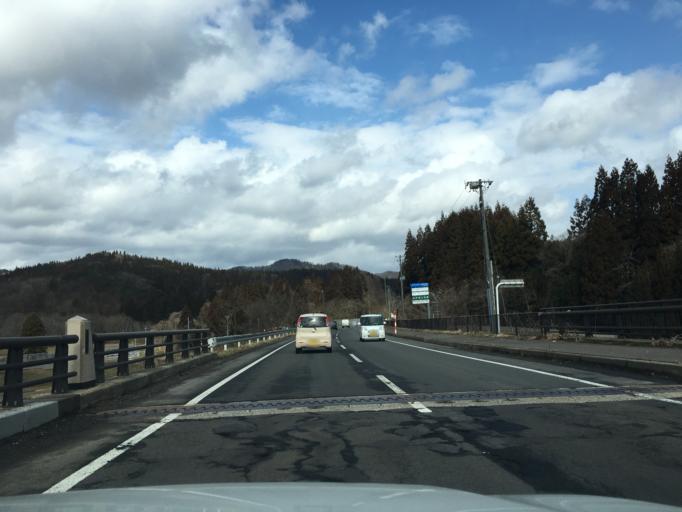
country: JP
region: Akita
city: Takanosu
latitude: 40.0259
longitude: 140.2739
